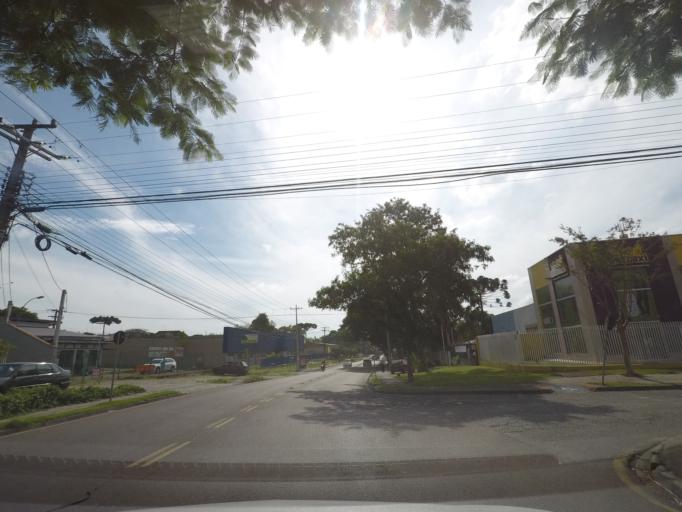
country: BR
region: Parana
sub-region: Curitiba
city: Curitiba
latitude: -25.4647
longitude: -49.2444
